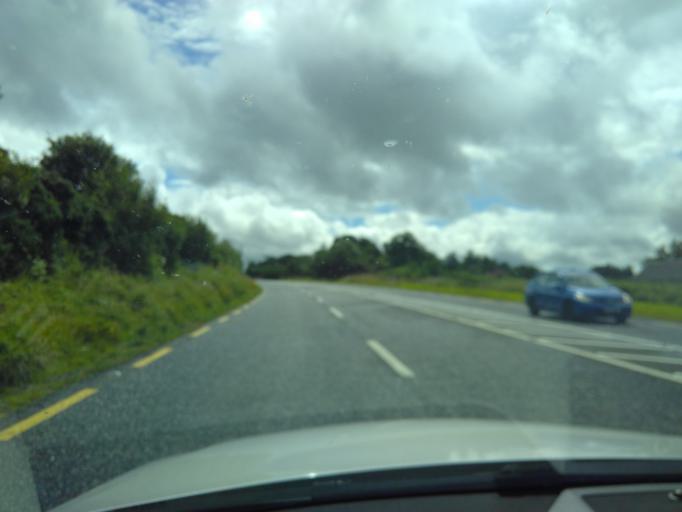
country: IE
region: Ulster
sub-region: County Donegal
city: Letterkenny
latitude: 54.9279
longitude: -7.6957
